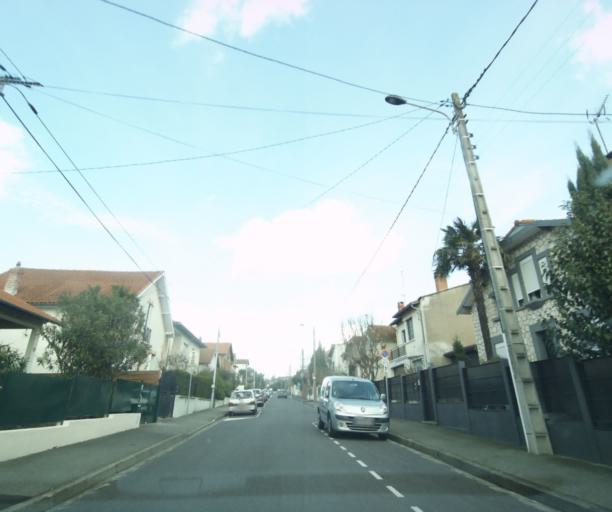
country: FR
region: Midi-Pyrenees
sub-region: Departement de la Haute-Garonne
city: Toulouse
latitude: 43.5849
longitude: 1.4712
